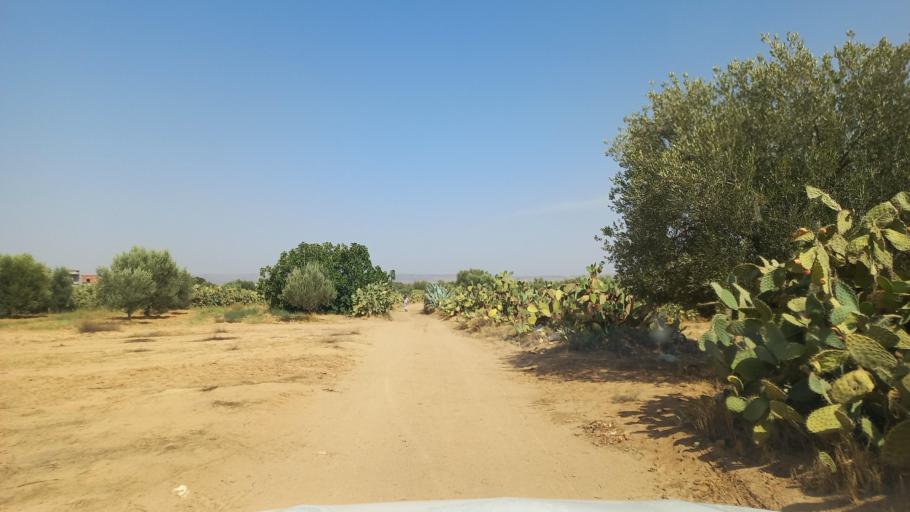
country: TN
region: Al Qasrayn
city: Kasserine
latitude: 35.2410
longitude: 9.0496
